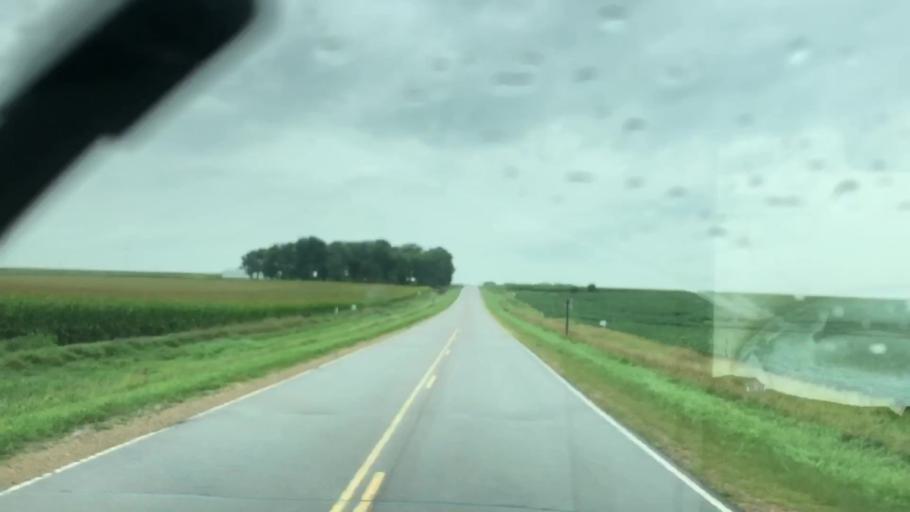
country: US
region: Iowa
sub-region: O'Brien County
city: Sanborn
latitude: 43.2367
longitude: -95.7235
